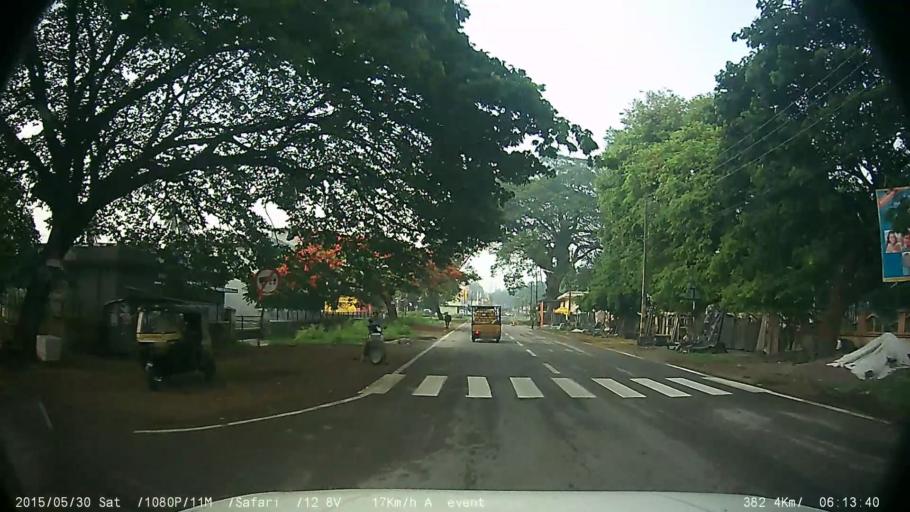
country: IN
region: Karnataka
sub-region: Mysore
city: Mysore
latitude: 12.3328
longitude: 76.6578
